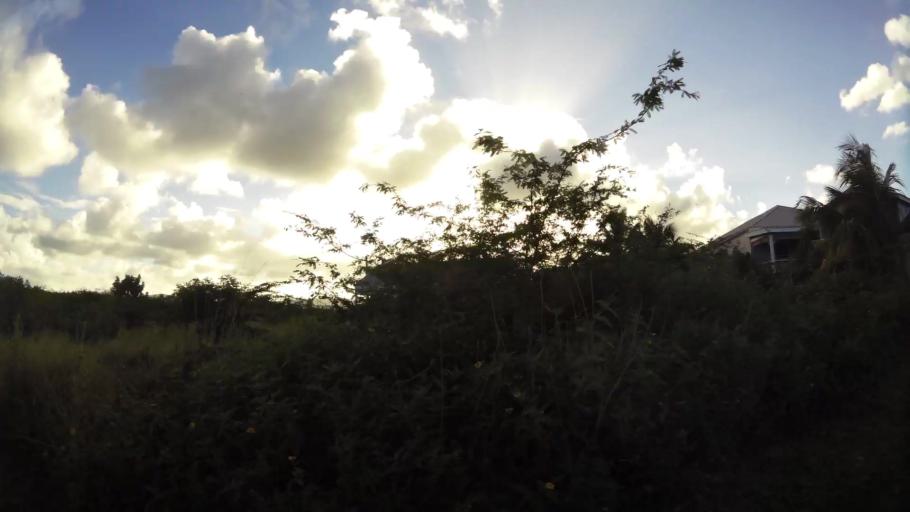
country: AG
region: Saint George
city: Piggotts
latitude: 17.1135
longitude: -61.7913
